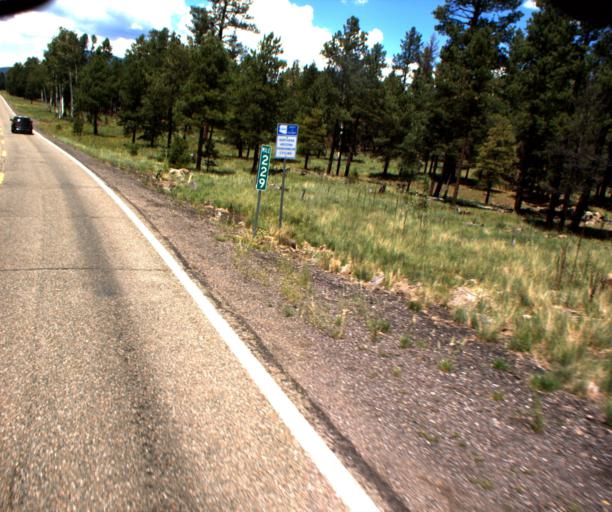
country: US
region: Arizona
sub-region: Coconino County
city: Flagstaff
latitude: 35.3259
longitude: -111.7736
